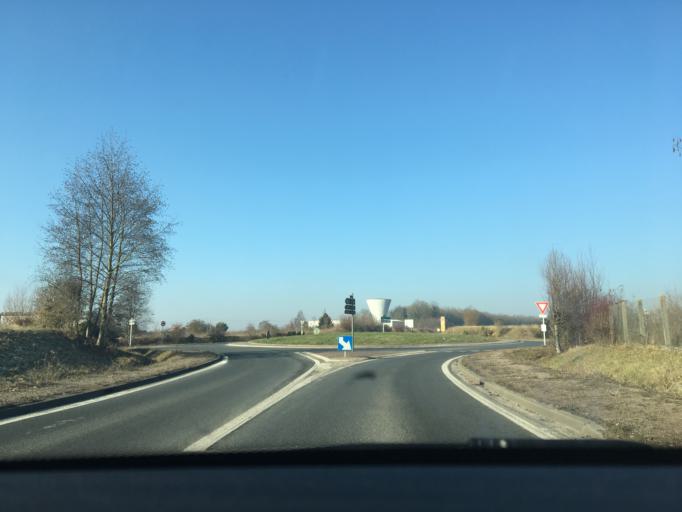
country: FR
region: Ile-de-France
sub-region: Departement des Yvelines
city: Limay
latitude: 49.0054
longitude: 1.7417
